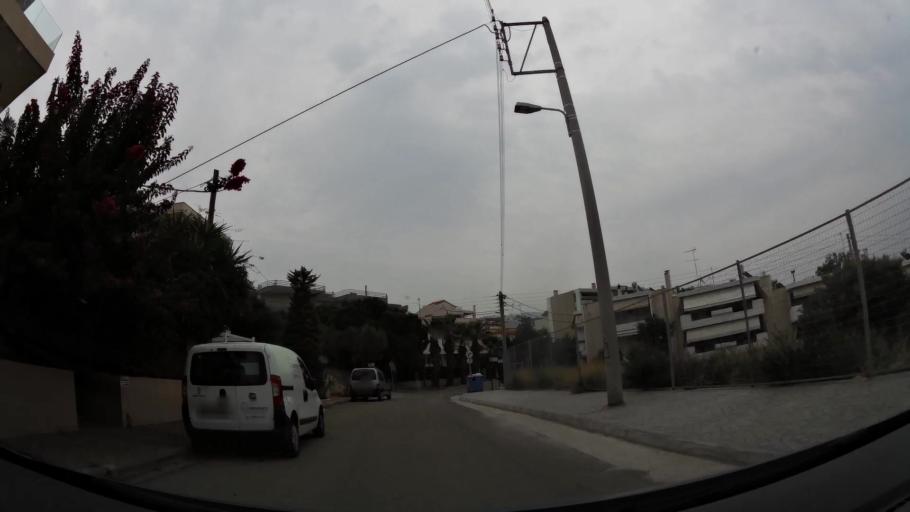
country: GR
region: Attica
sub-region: Nomarchia Athinas
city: Alimos
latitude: 37.9095
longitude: 23.7233
